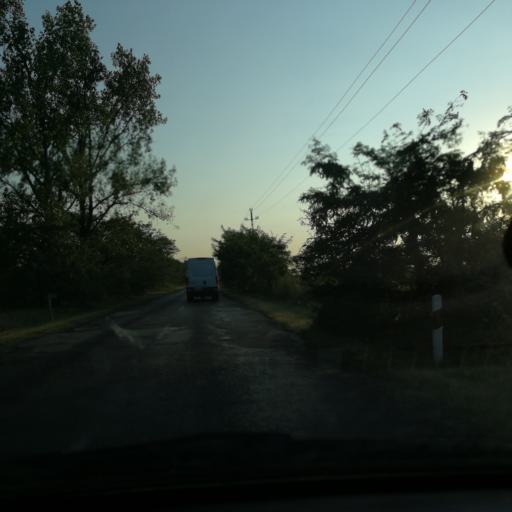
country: HU
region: Bacs-Kiskun
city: Kiskunhalas
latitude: 46.4417
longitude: 19.5720
